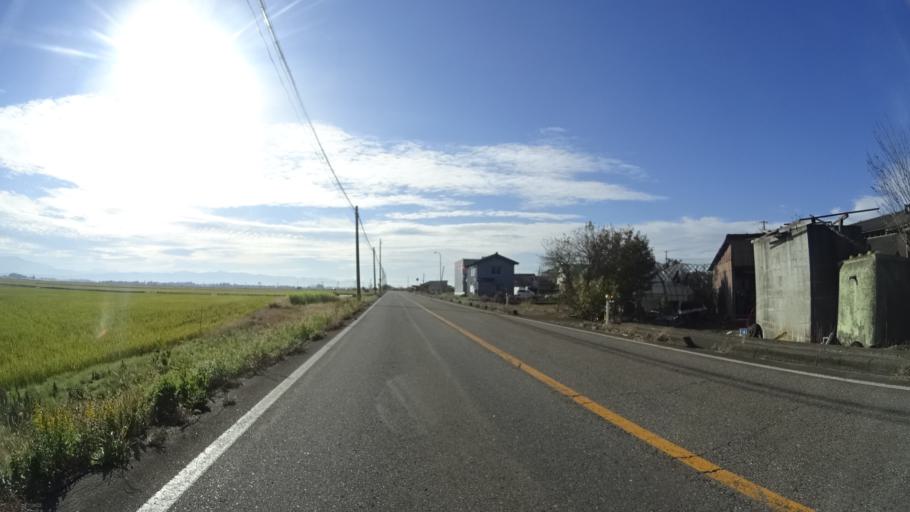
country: JP
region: Niigata
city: Mitsuke
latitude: 37.5729
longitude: 138.8415
